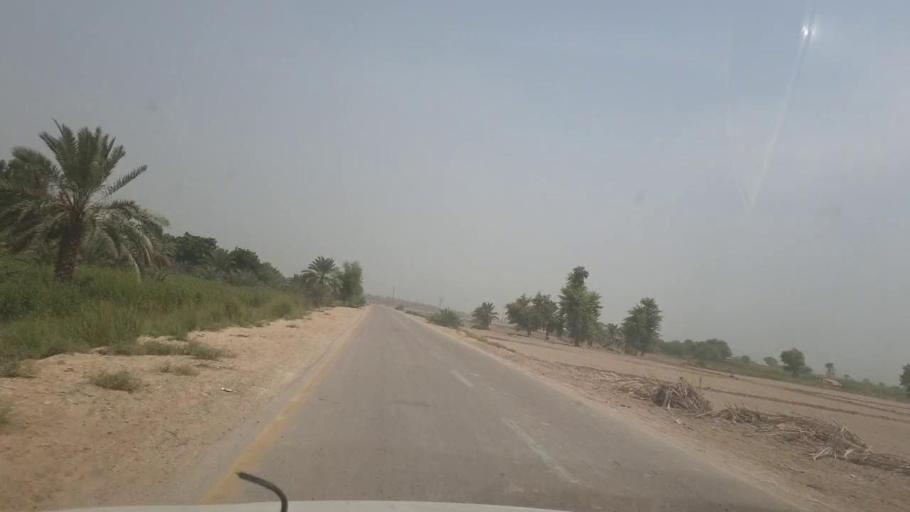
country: PK
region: Sindh
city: Kot Diji
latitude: 27.3979
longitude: 68.6606
